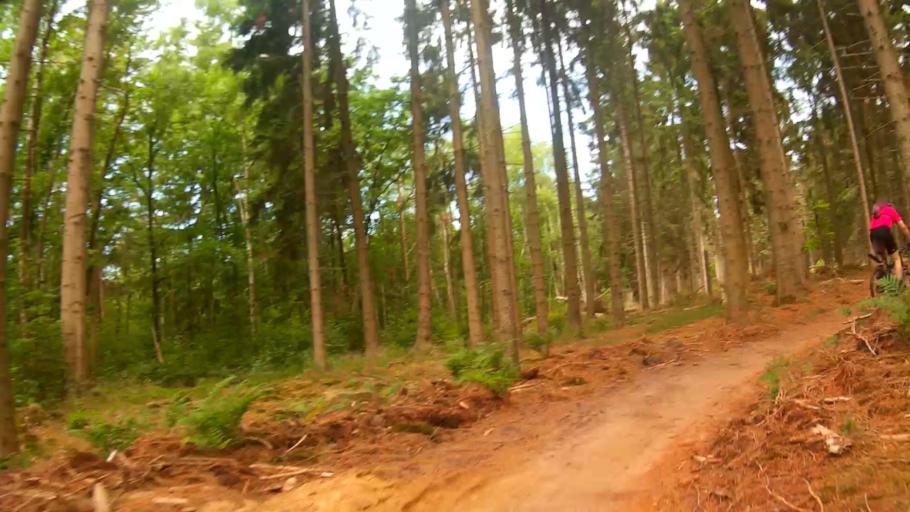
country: NL
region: Utrecht
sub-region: Gemeente Soest
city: Soest
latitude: 52.1802
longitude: 5.2350
